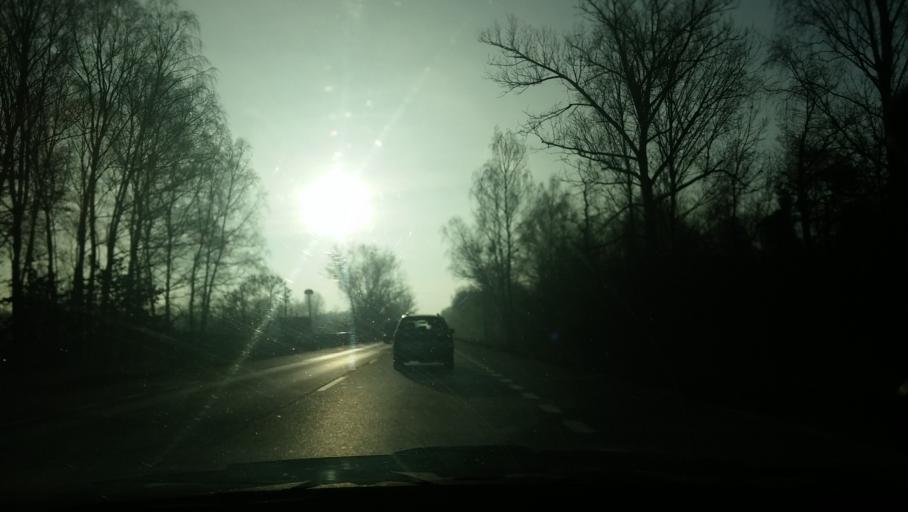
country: PL
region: Masovian Voivodeship
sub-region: Powiat minski
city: Sulejowek
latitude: 52.2152
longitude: 21.2567
